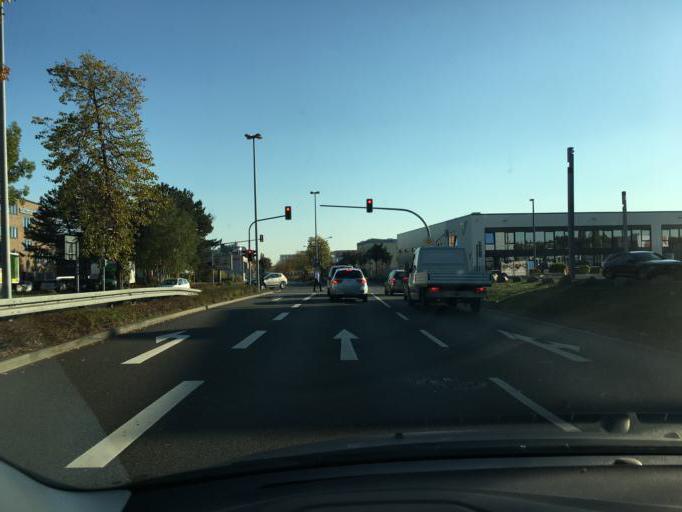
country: DE
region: Saxony
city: Leipzig
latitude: 51.3701
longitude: 12.3972
